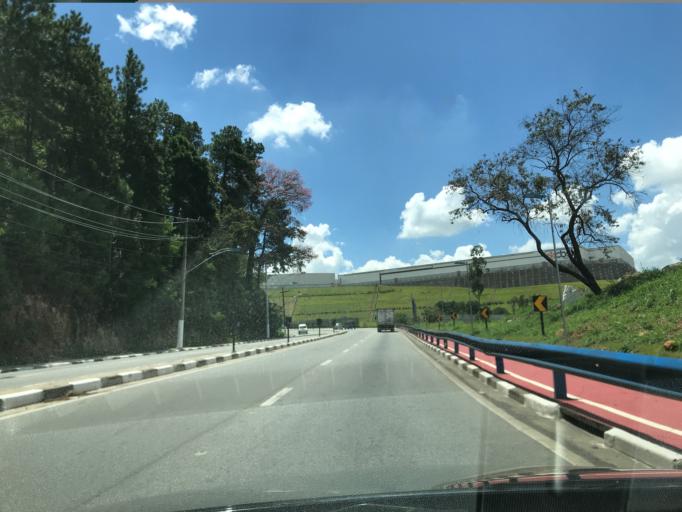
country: BR
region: Sao Paulo
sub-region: Itapevi
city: Itapevi
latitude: -23.5326
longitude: -46.9364
